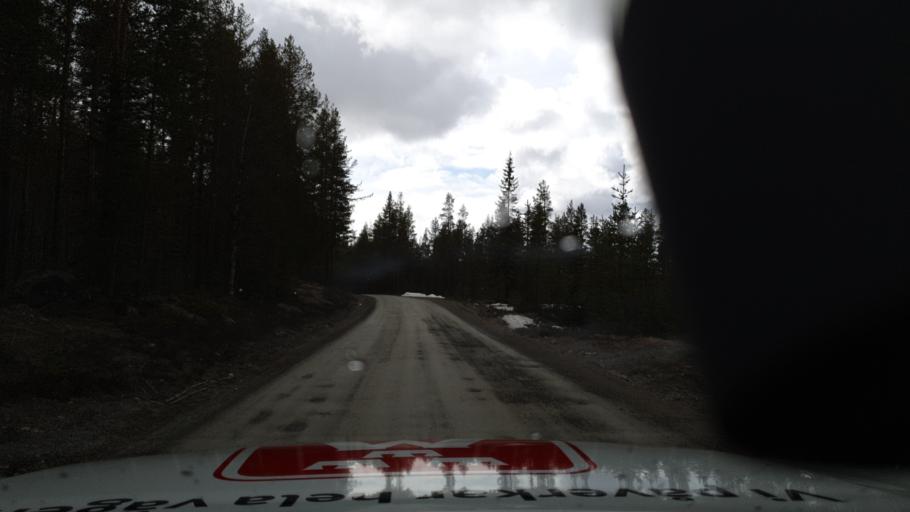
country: SE
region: Jaemtland
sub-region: Bergs Kommun
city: Hoverberg
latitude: 62.7861
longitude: 13.8240
